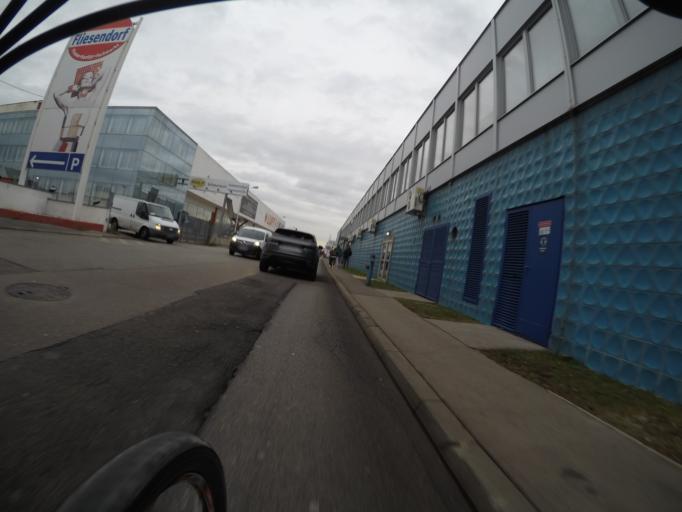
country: AT
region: Lower Austria
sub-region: Politischer Bezirk Modling
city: Vosendorf
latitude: 48.1263
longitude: 16.3225
